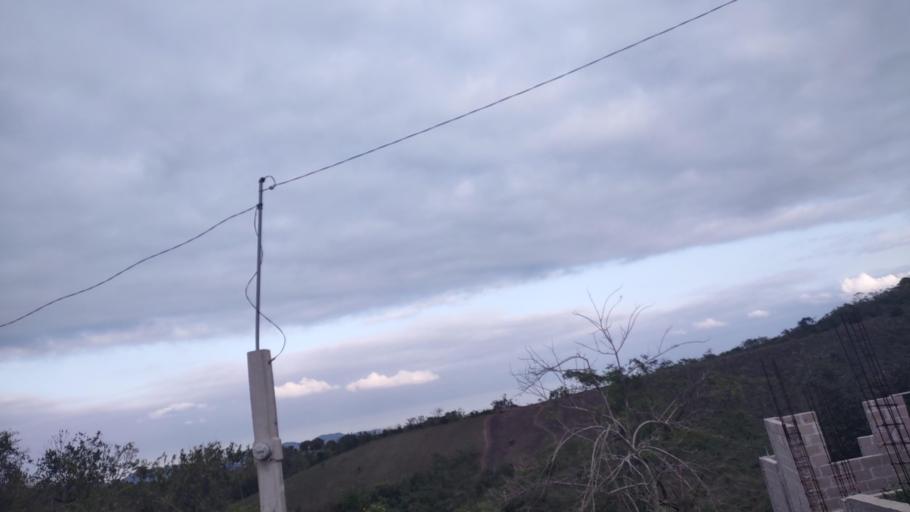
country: MX
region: Veracruz
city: Papantla de Olarte
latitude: 20.4539
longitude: -97.3102
